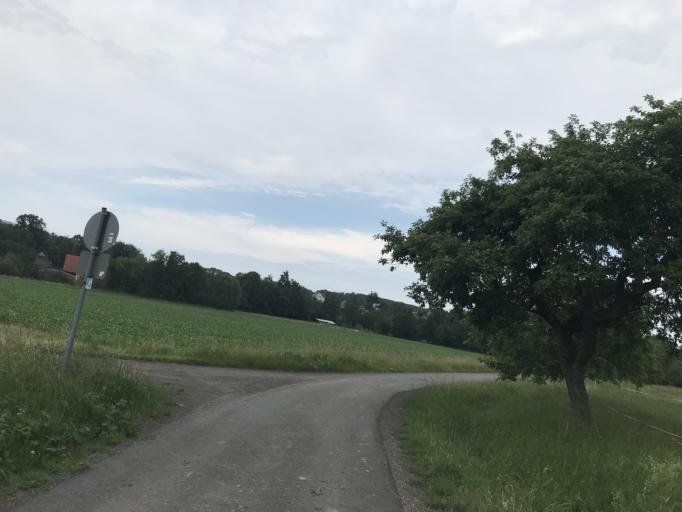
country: DE
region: Hesse
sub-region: Regierungsbezirk Giessen
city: Laubach
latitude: 50.5136
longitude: 8.9546
